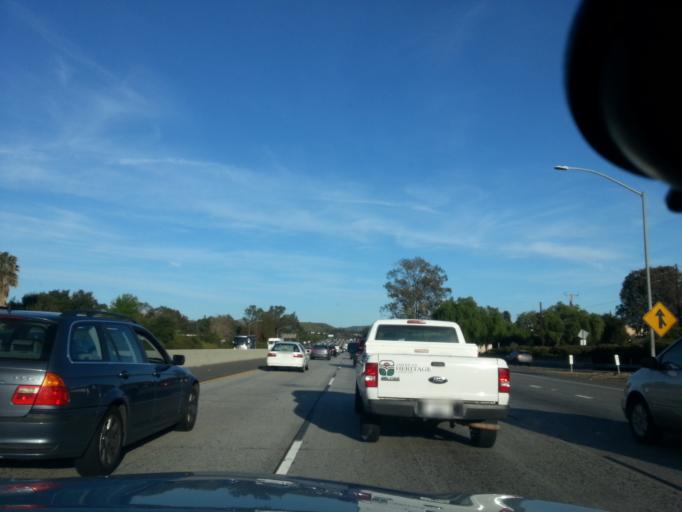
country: US
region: California
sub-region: Ventura County
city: Casa Conejo
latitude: 34.1843
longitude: -118.9096
